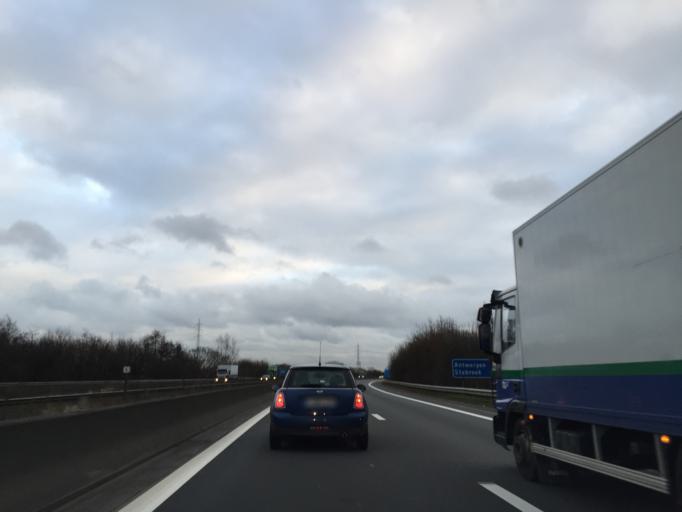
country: BE
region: Flanders
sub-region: Provincie Antwerpen
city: Stabroek
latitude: 51.3502
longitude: 4.3430
